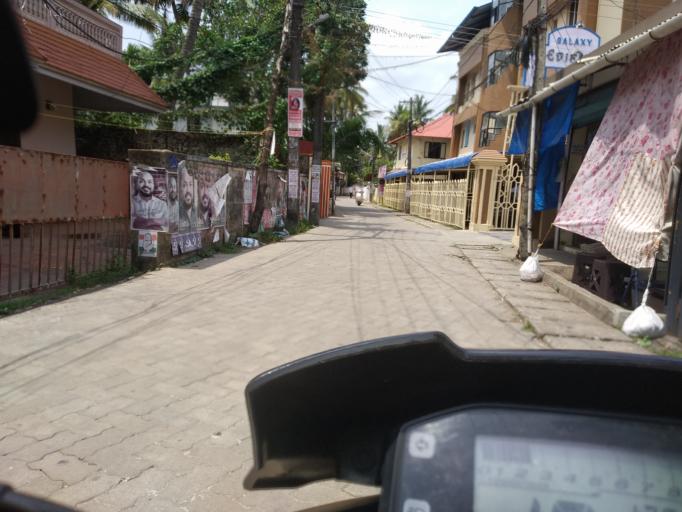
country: IN
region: Kerala
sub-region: Ernakulam
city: Elur
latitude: 10.0162
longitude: 76.3266
